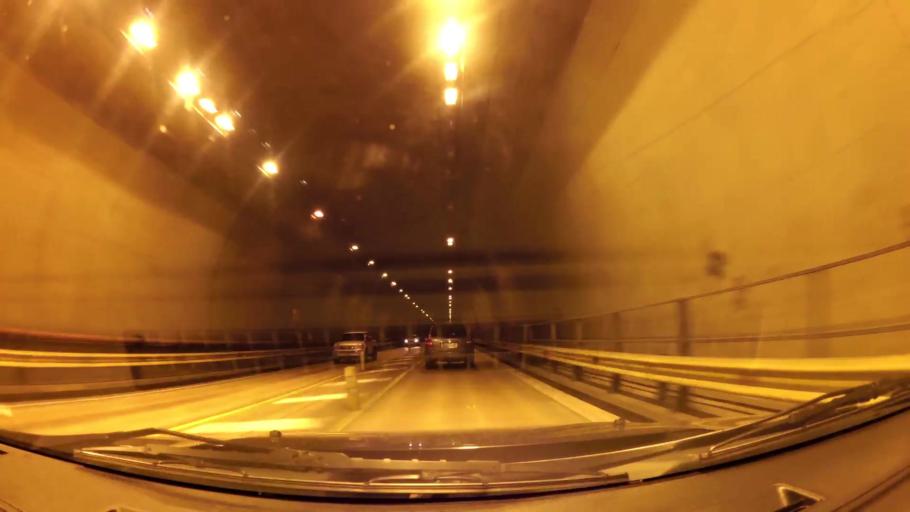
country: EC
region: Pichincha
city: Quito
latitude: -0.1899
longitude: -78.4771
